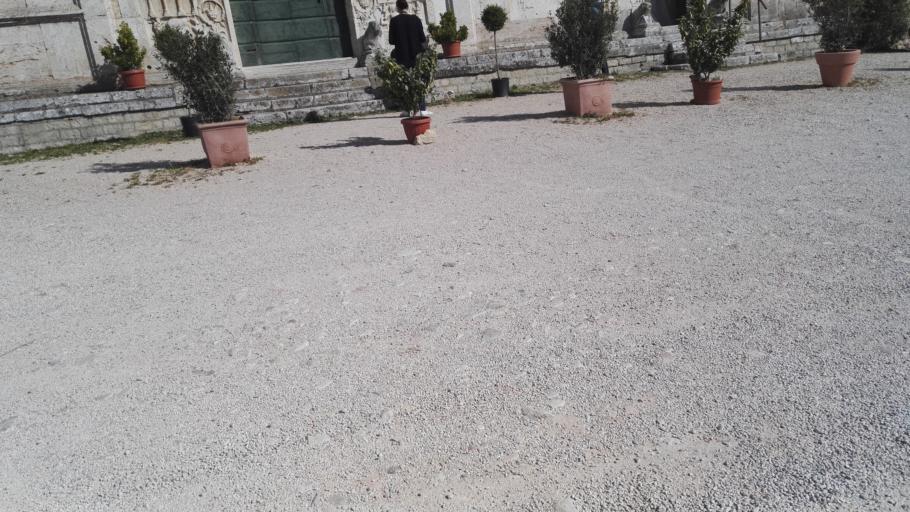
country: IT
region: Umbria
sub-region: Provincia di Perugia
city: Spoleto
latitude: 42.7271
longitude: 12.7375
